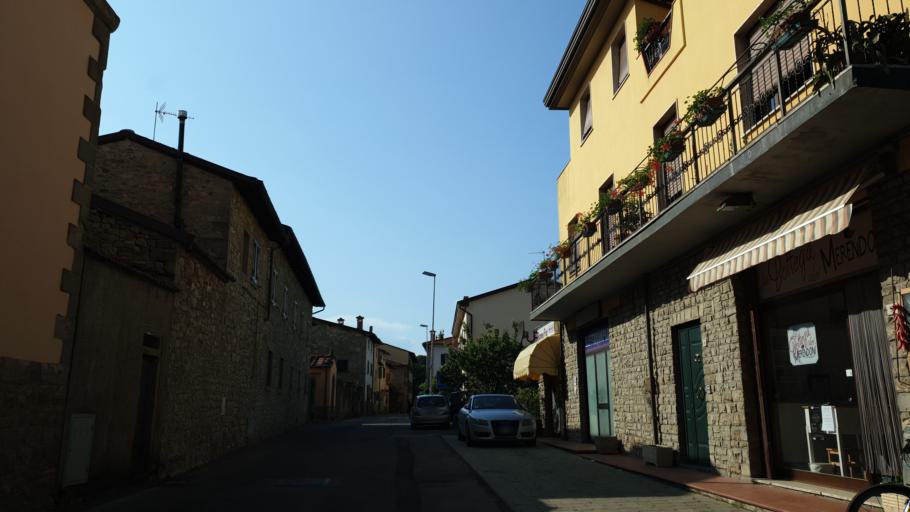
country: IT
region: Tuscany
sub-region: Province of Arezzo
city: Strada
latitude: 43.7502
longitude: 11.7244
